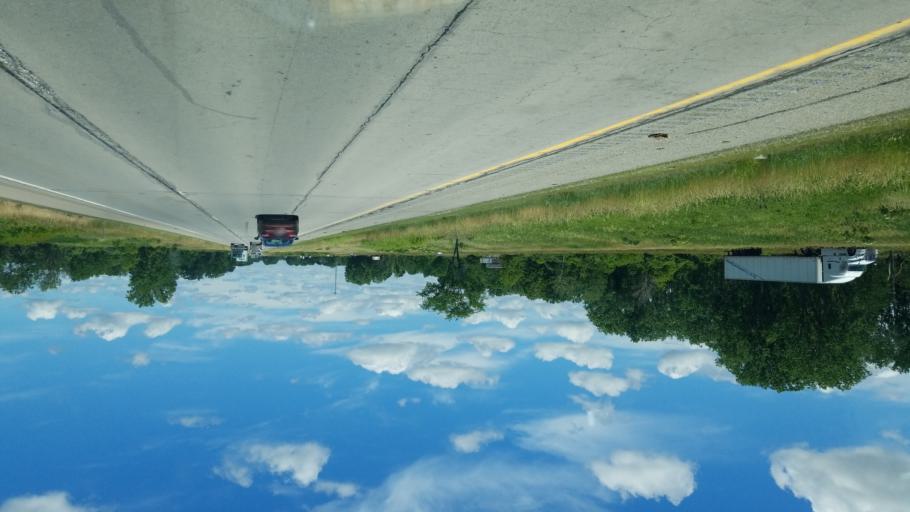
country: US
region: Michigan
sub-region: Livingston County
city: Fowlerville
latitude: 42.6275
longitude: -84.0065
